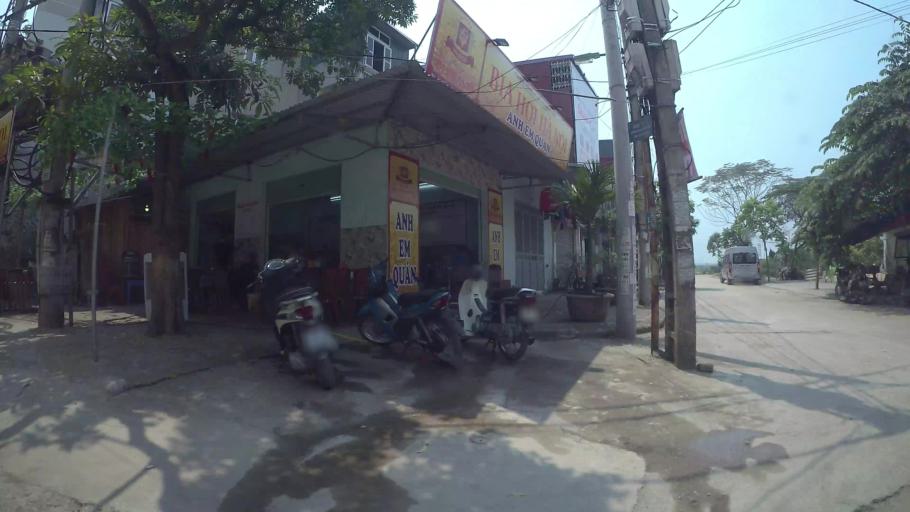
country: VN
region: Ha Noi
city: Van Dien
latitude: 20.9493
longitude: 105.8250
